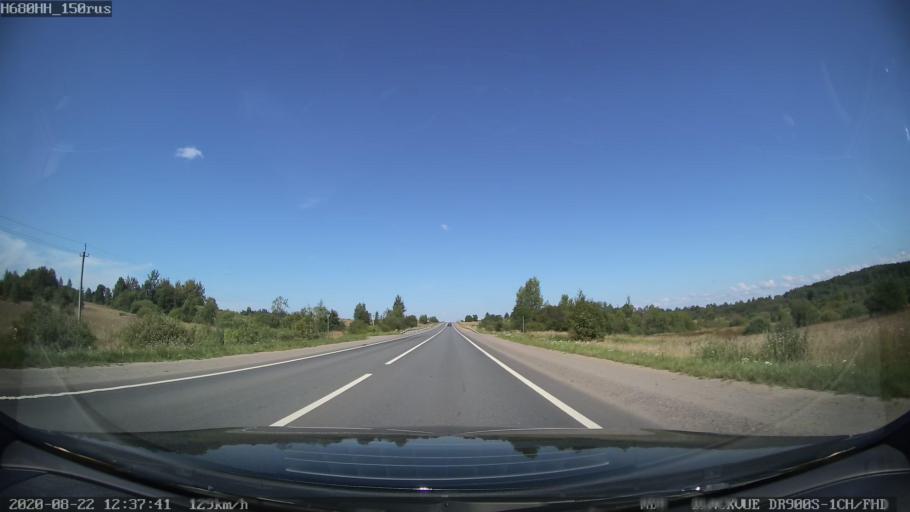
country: RU
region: Tverskaya
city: Rameshki
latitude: 57.3006
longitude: 36.0889
